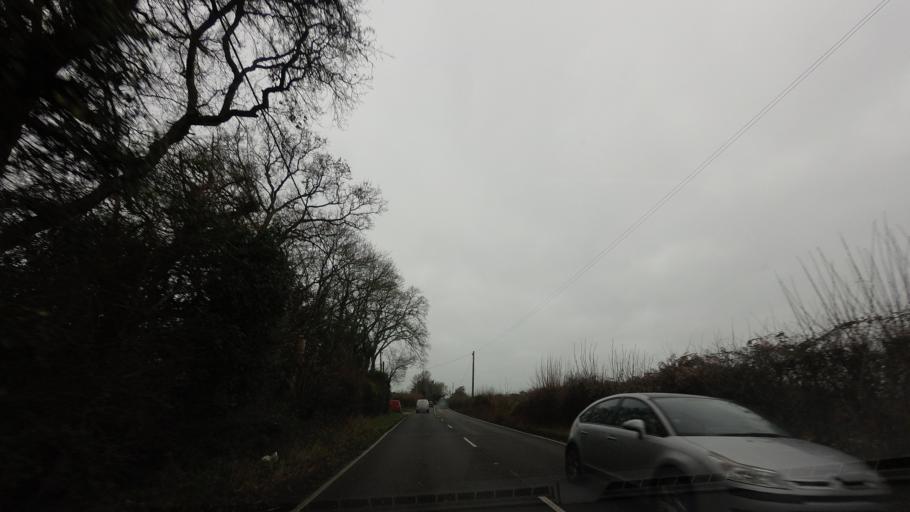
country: GB
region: England
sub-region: East Sussex
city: Battle
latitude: 50.9387
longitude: 0.5160
